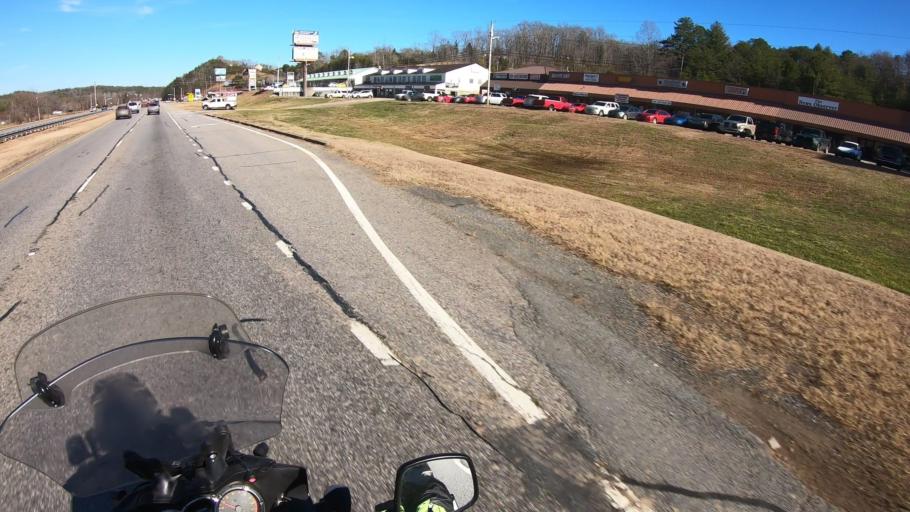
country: US
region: Georgia
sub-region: Fannin County
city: Blue Ridge
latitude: 34.8789
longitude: -84.2965
